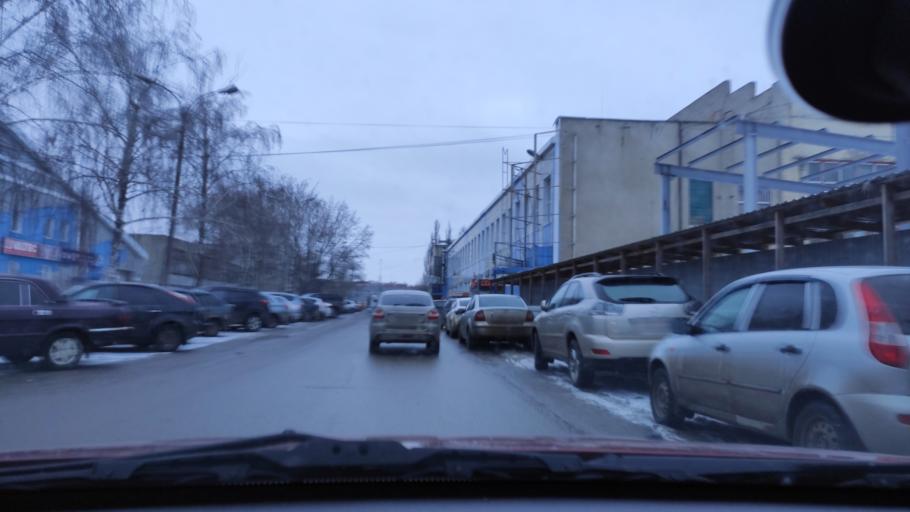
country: RU
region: Tambov
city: Tambov
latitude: 52.7544
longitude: 41.4508
